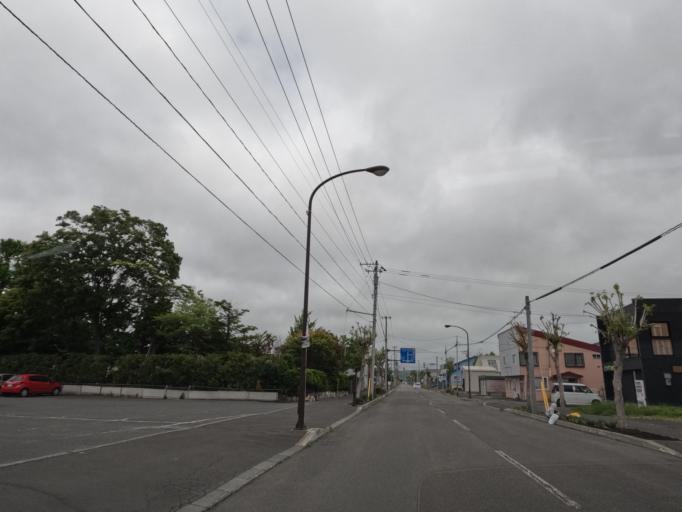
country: JP
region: Hokkaido
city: Tobetsu
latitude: 43.2245
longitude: 141.5179
